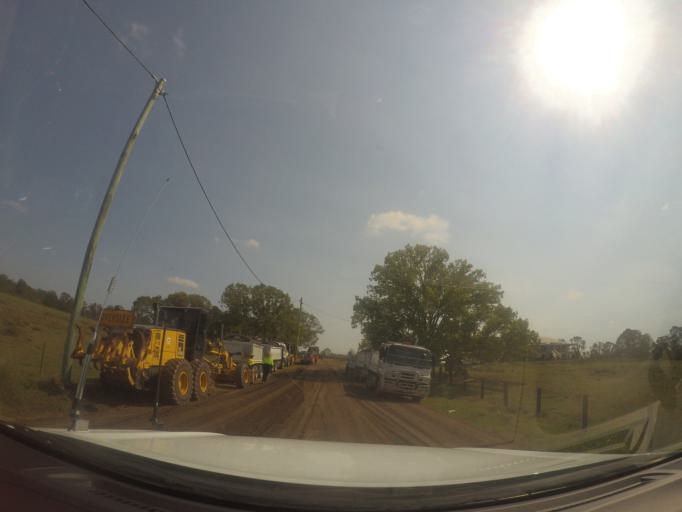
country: AU
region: Queensland
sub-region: Logan
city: Chambers Flat
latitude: -27.7557
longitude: 153.0602
